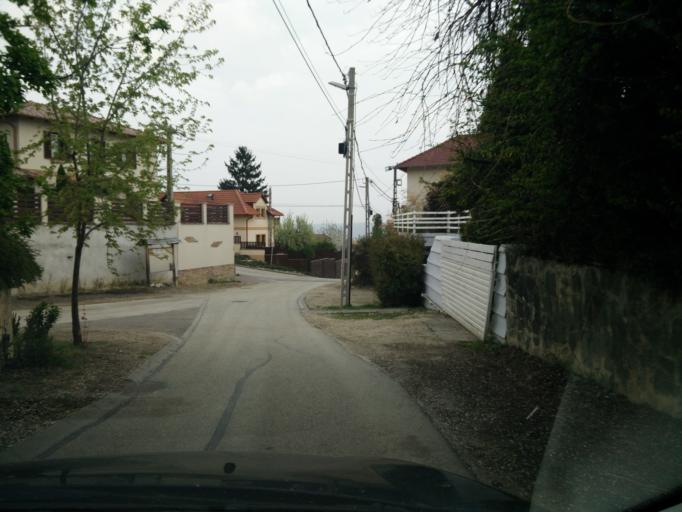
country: HU
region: Pest
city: Budaors
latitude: 47.4682
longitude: 18.9579
